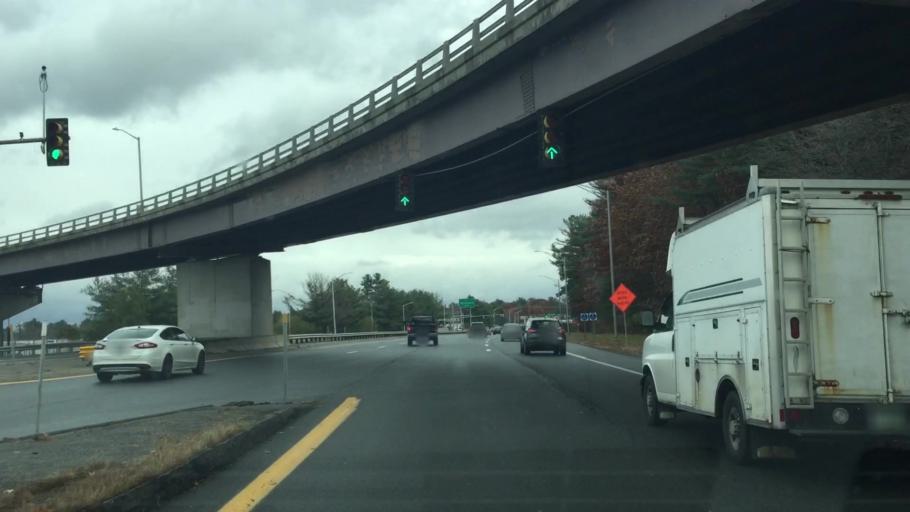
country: US
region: New Hampshire
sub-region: Rockingham County
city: Salem
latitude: 42.7662
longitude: -71.2274
